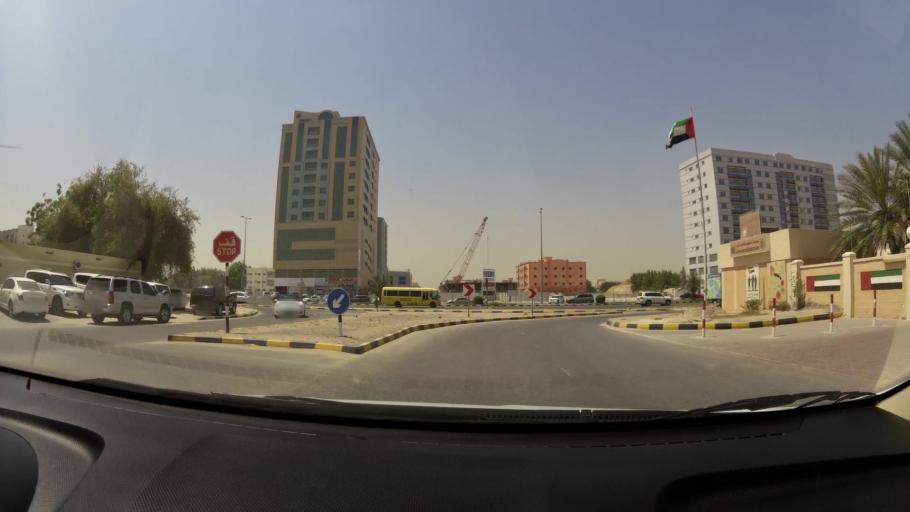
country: AE
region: Ajman
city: Ajman
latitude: 25.3995
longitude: 55.5082
